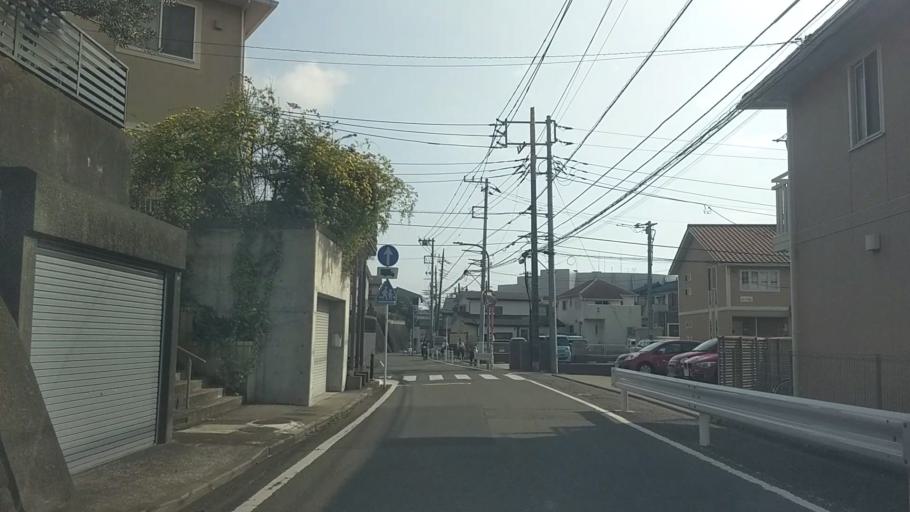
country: JP
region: Kanagawa
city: Kamakura
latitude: 35.3706
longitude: 139.5551
